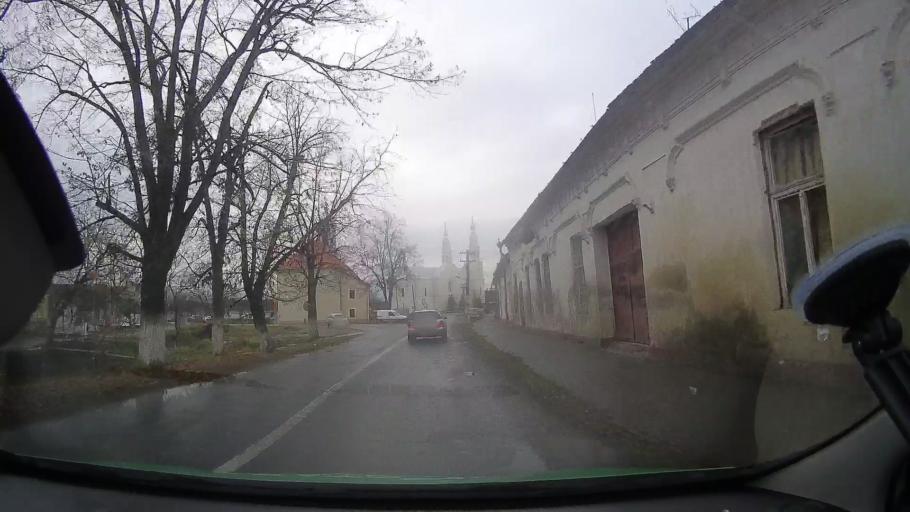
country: RO
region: Arad
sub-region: Comuna Buteni
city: Buteni
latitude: 46.3290
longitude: 22.1238
